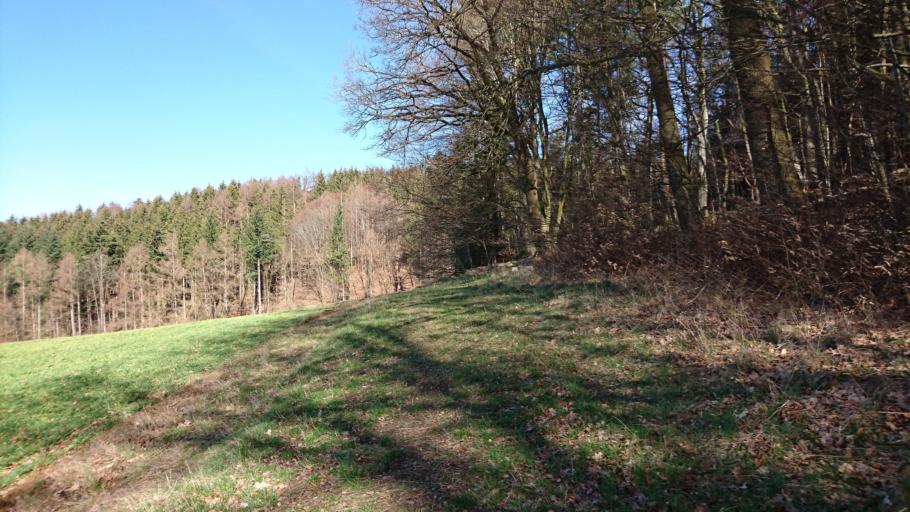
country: DE
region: Bavaria
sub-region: Swabia
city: Altenmunster
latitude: 48.4526
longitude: 10.6012
